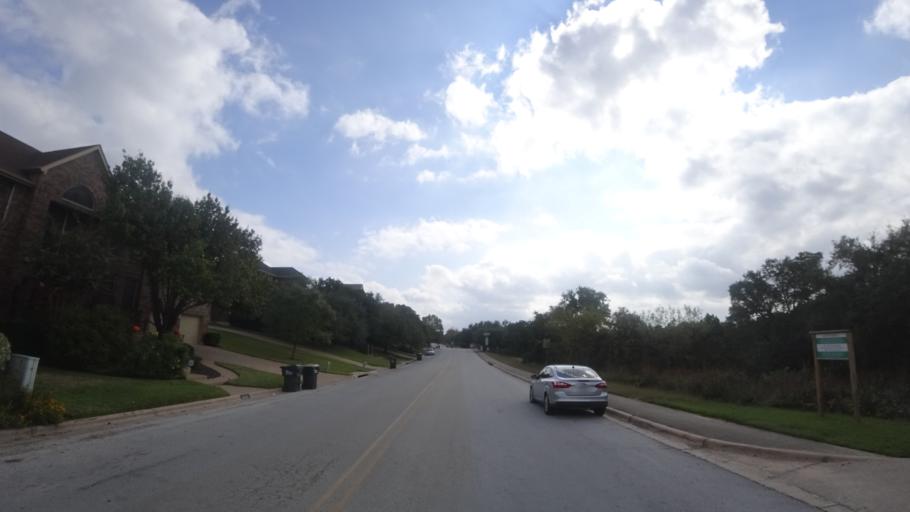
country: US
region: Texas
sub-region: Travis County
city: Barton Creek
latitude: 30.3039
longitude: -97.8884
